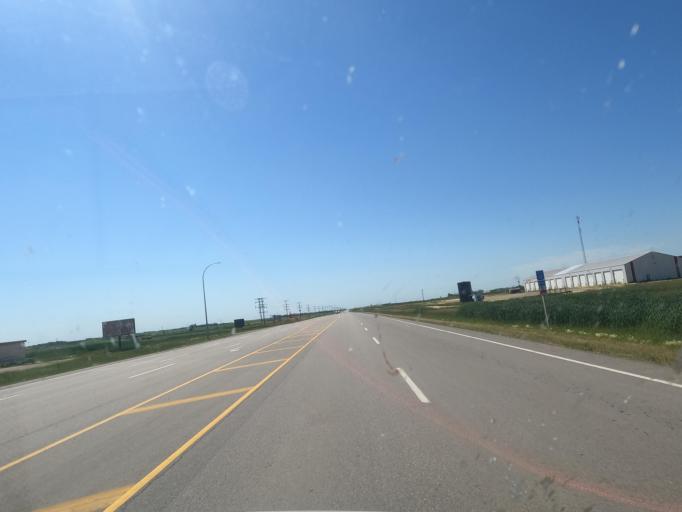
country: CA
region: Saskatchewan
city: Estevan
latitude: 49.6686
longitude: -103.0239
